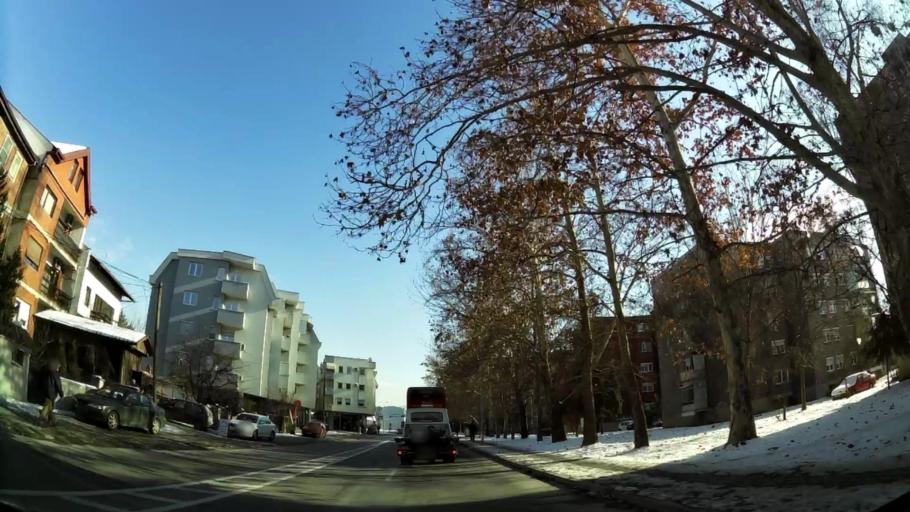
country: MK
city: Krushopek
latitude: 42.0046
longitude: 21.3722
